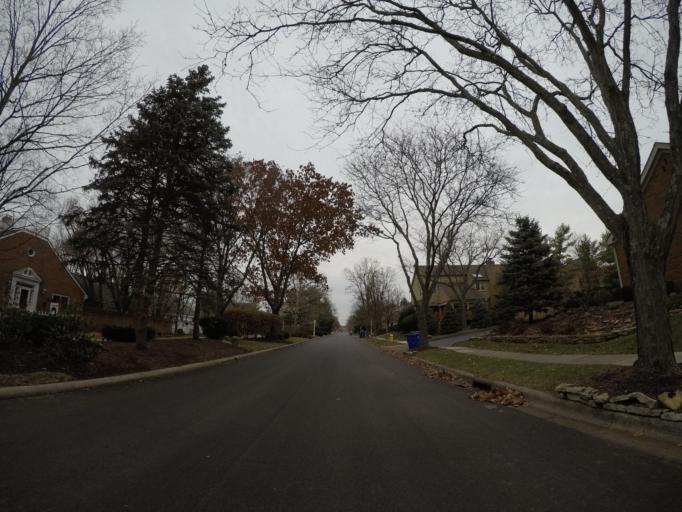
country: US
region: Ohio
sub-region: Franklin County
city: Dublin
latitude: 40.0546
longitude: -83.0793
